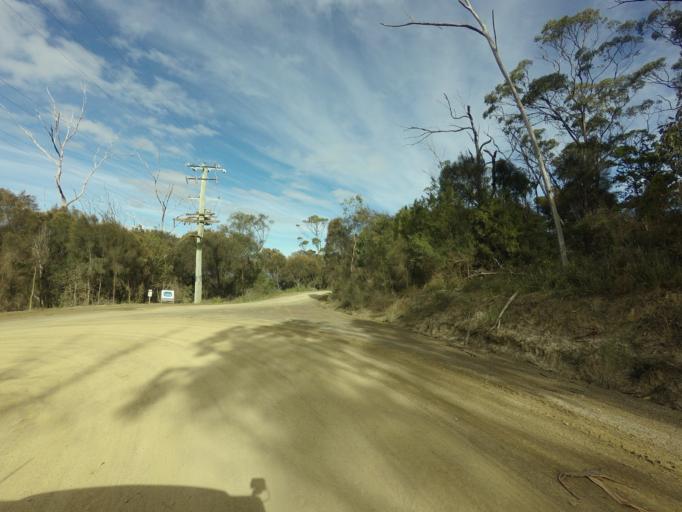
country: AU
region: Tasmania
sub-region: Clarence
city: Sandford
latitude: -43.0956
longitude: 147.7195
